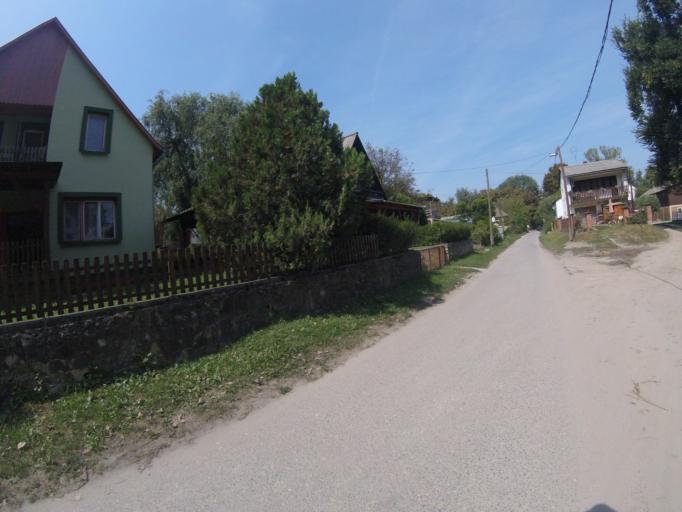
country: HU
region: Bacs-Kiskun
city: Baja
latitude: 46.1938
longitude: 18.9228
